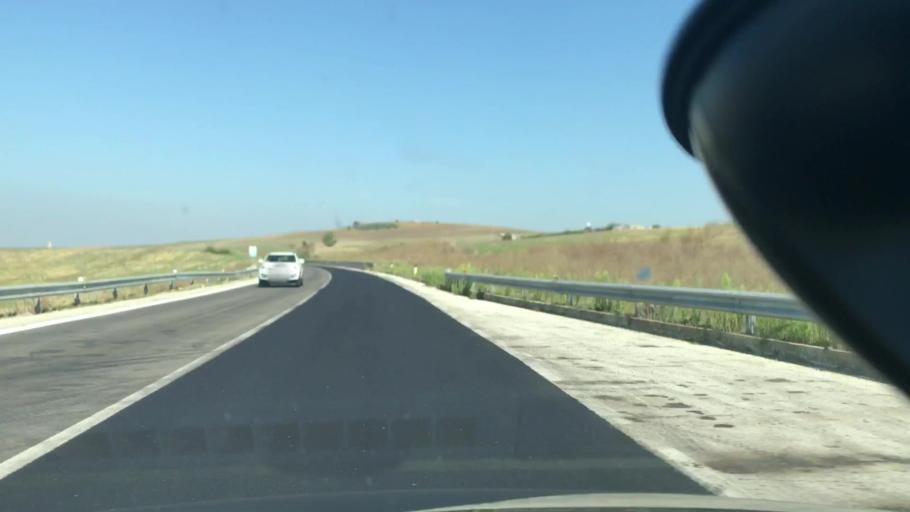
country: IT
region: Apulia
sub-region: Provincia di Barletta - Andria - Trani
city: Spinazzola
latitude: 40.9188
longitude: 16.0998
